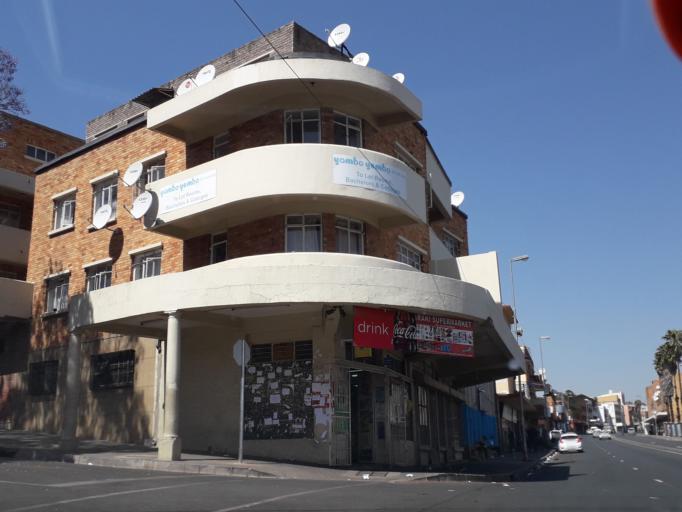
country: ZA
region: Gauteng
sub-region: City of Johannesburg Metropolitan Municipality
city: Johannesburg
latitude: -26.1643
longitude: 28.0826
